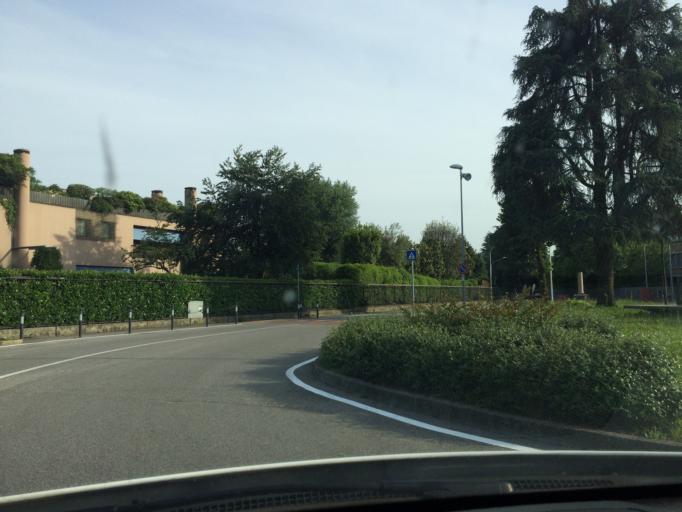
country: IT
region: Veneto
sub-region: Provincia di Padova
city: Cittadella
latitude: 45.6512
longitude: 11.7774
